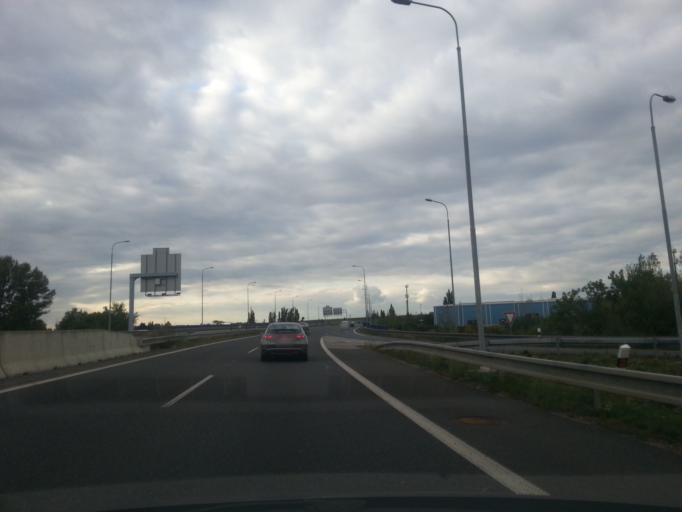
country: CZ
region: Central Bohemia
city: Hostivice
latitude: 50.0765
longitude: 14.2884
